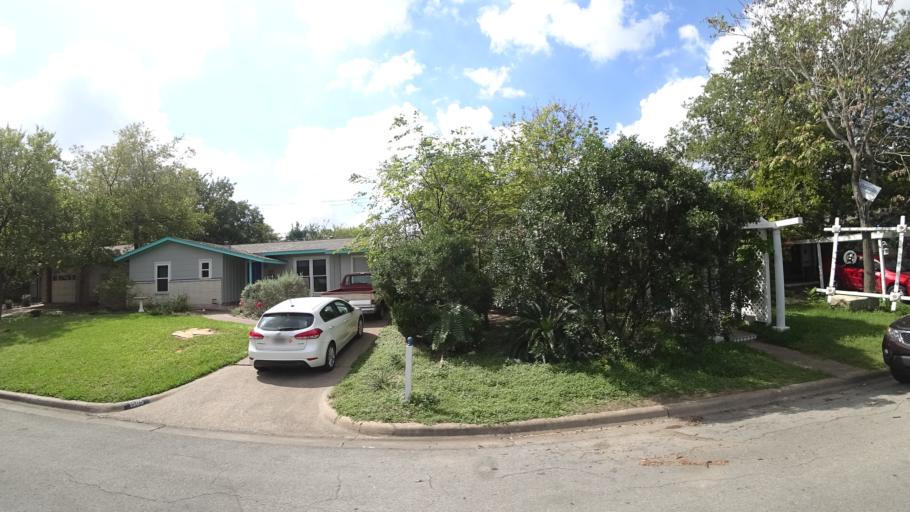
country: US
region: Texas
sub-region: Travis County
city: Wells Branch
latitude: 30.3606
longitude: -97.7181
